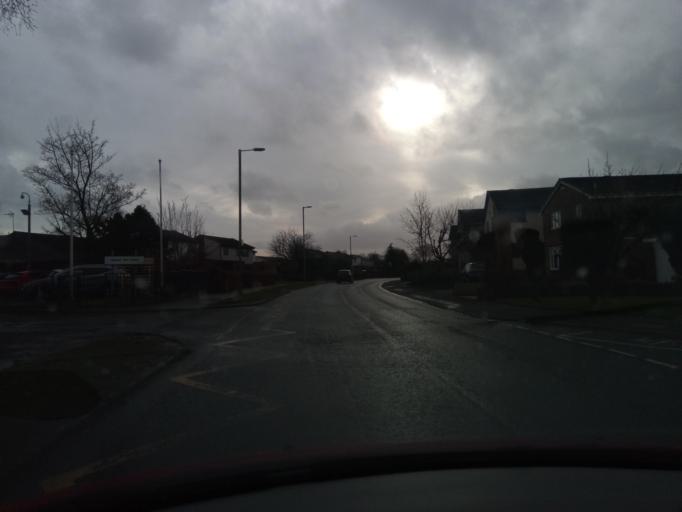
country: GB
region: Scotland
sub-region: East Dunbartonshire
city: Kirkintilloch
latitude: 55.9229
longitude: -4.1737
